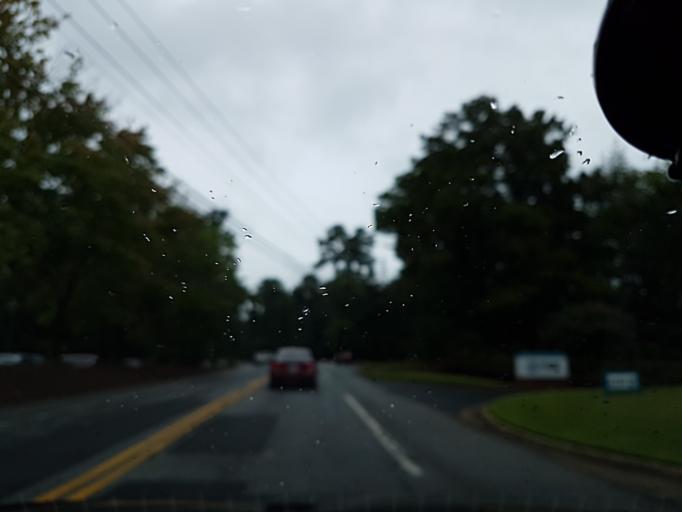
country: US
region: Georgia
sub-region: Gwinnett County
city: Norcross
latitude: 33.9538
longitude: -84.2413
